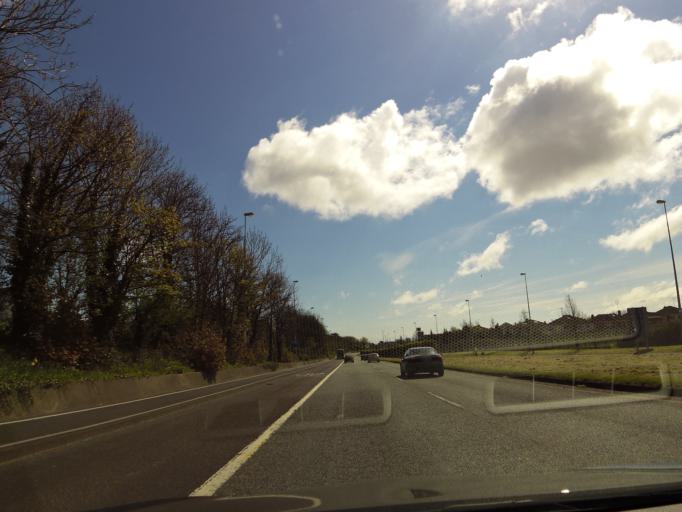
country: IE
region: Leinster
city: Cabinteely
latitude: 53.2702
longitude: -6.1649
